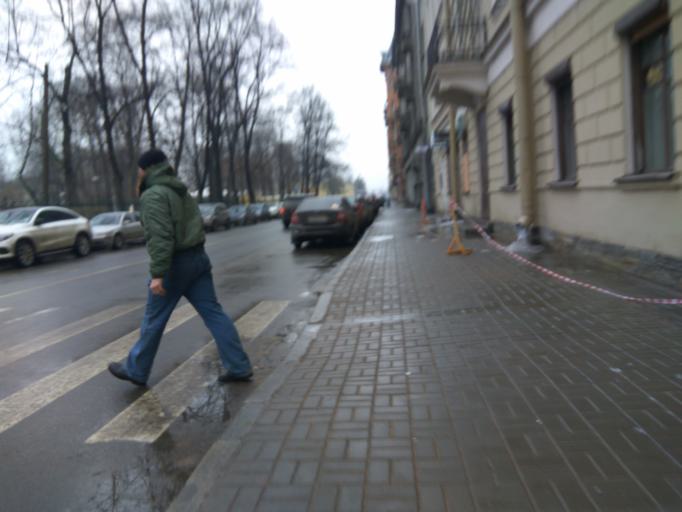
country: RU
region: St.-Petersburg
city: Centralniy
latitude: 59.9455
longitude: 30.3782
